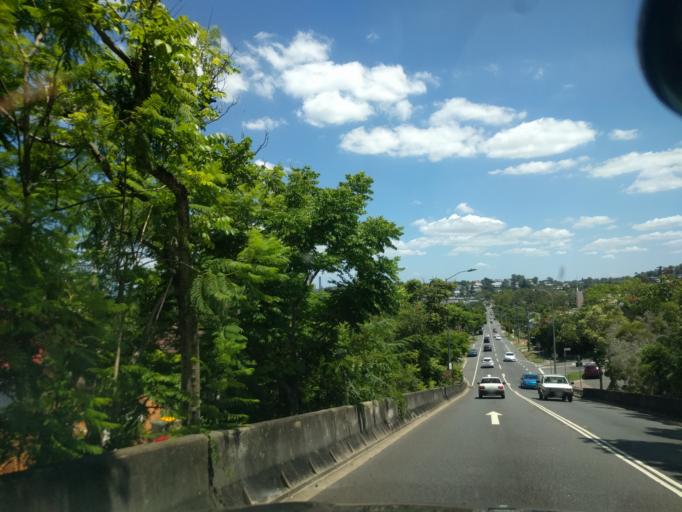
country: AU
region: Queensland
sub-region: Brisbane
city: Stafford
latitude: -27.4020
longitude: 153.0093
